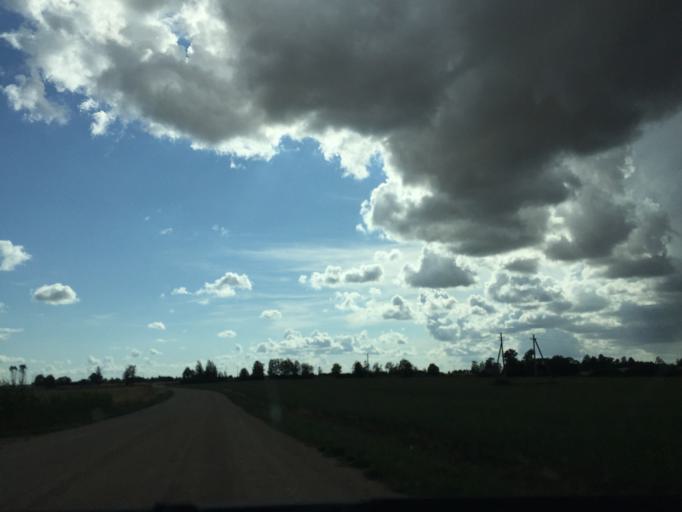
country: LV
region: Tervete
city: Zelmeni
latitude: 56.3029
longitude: 23.4132
